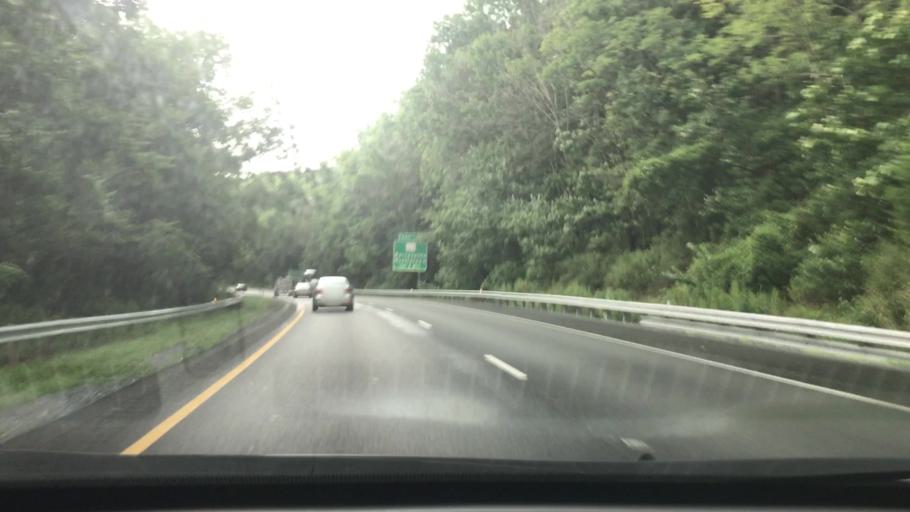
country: US
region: Maryland
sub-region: Frederick County
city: Green Valley
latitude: 39.2698
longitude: -77.3138
